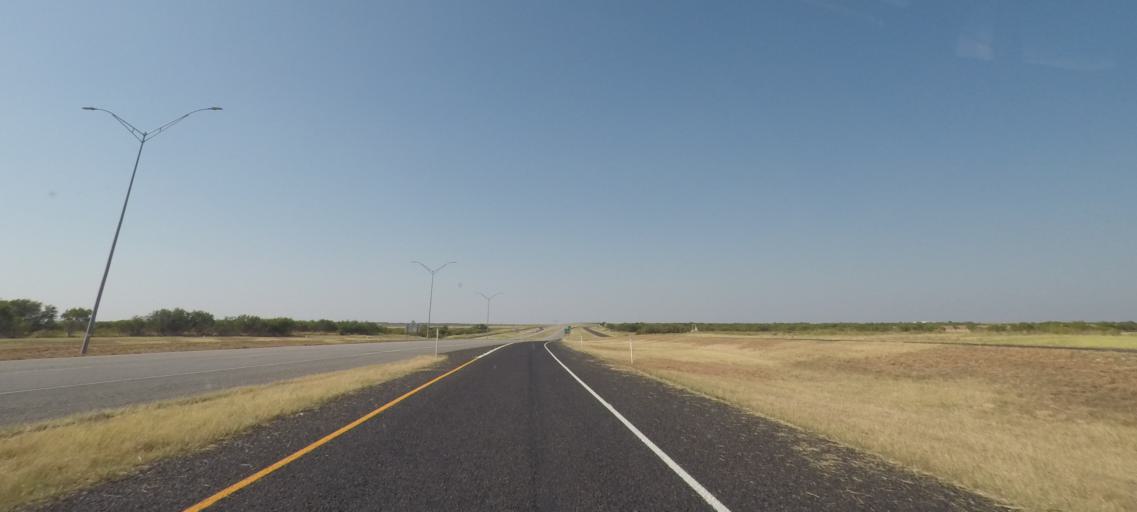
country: US
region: Texas
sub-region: Baylor County
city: Seymour
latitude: 33.6010
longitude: -99.2416
